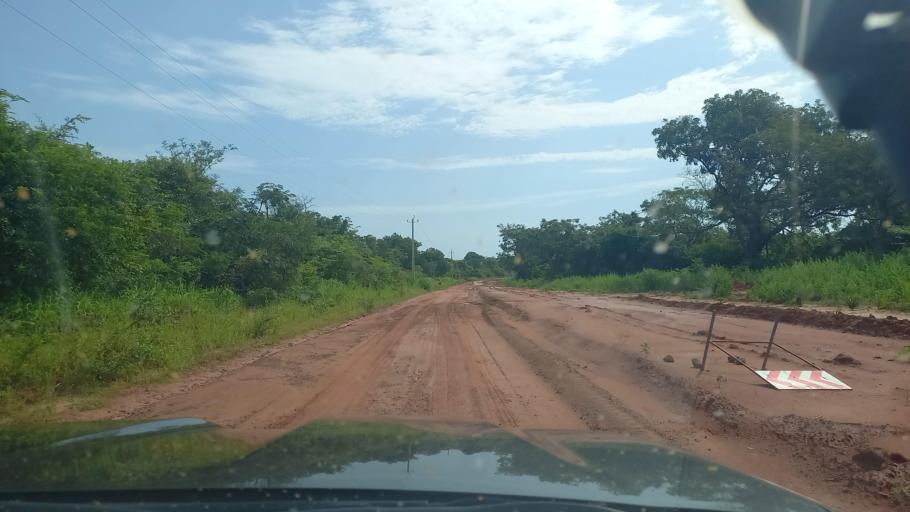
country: SN
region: Ziguinchor
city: Ziguinchor
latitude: 12.6709
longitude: -16.2202
